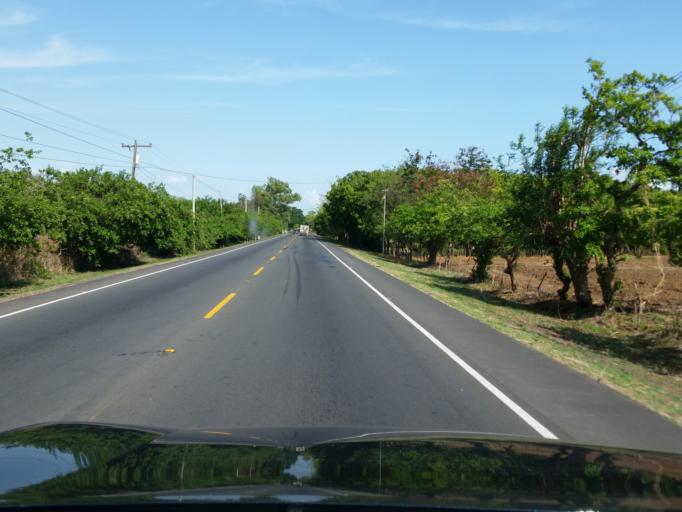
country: NI
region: Leon
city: Leon
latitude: 12.4061
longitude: -86.8589
